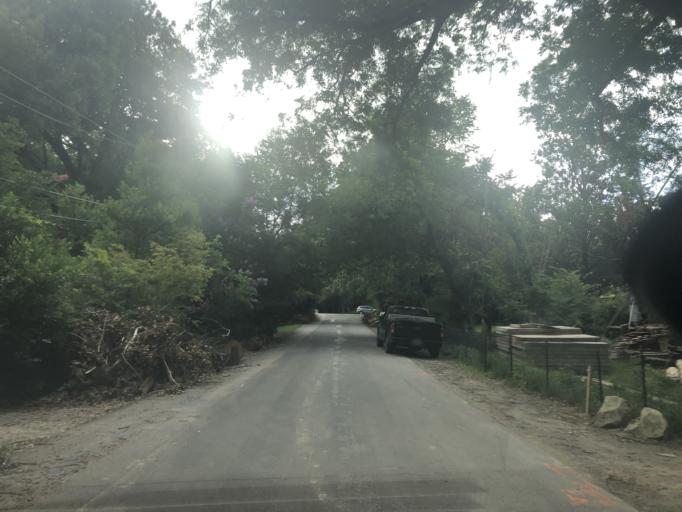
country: US
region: Texas
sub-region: Dallas County
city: University Park
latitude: 32.8587
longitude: -96.8387
